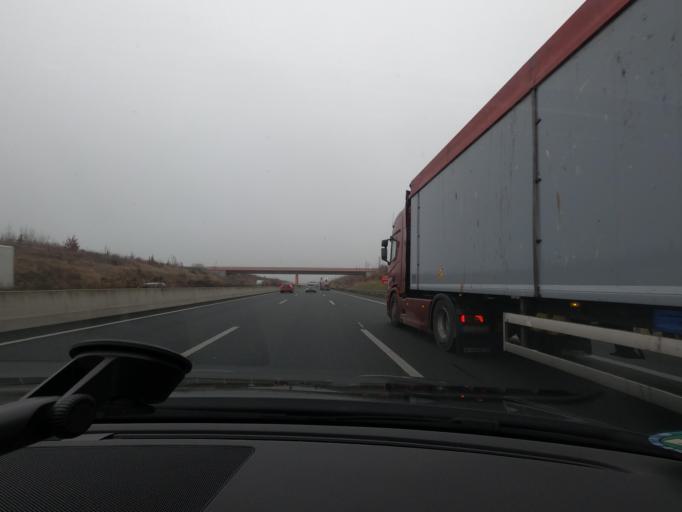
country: DE
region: North Rhine-Westphalia
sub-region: Regierungsbezirk Koln
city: Elsdorf
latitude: 50.8681
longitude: 6.5877
